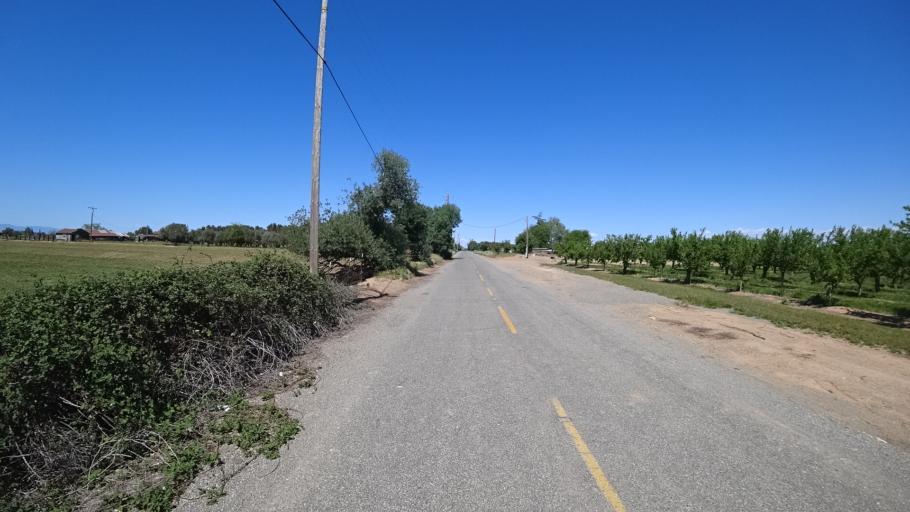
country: US
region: California
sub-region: Glenn County
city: Orland
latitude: 39.7793
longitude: -122.1782
